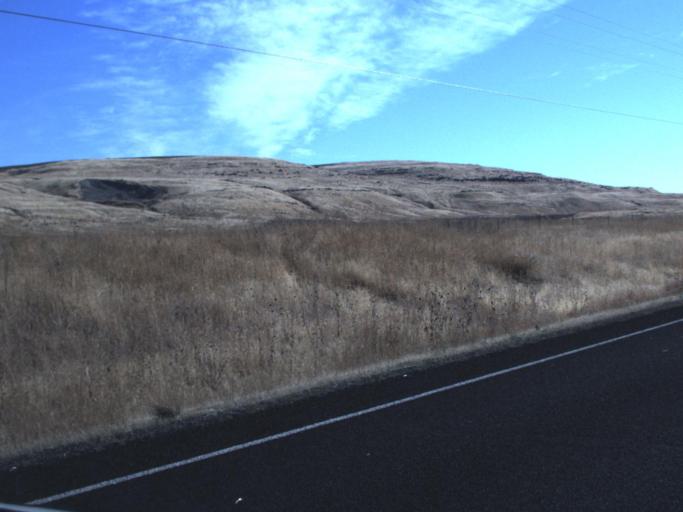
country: US
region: Washington
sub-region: Franklin County
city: Connell
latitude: 46.6491
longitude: -118.5949
